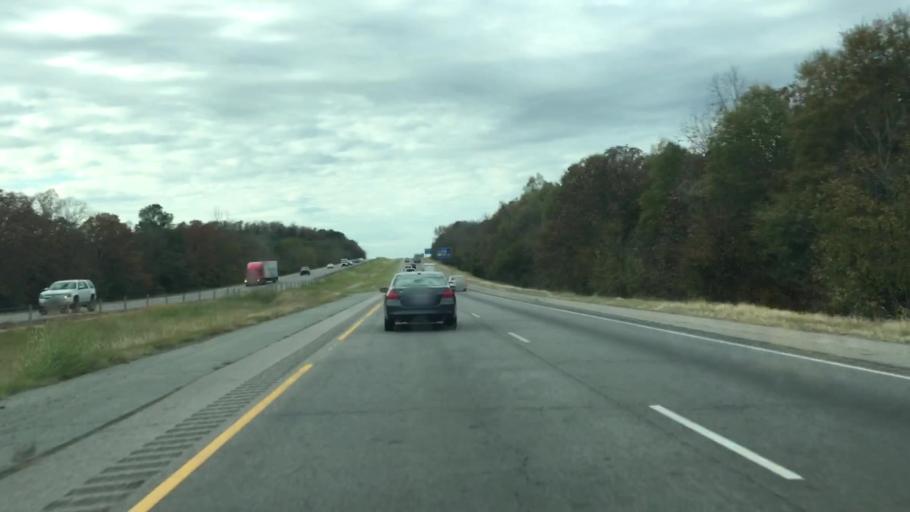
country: US
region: Arkansas
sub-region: Conway County
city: Morrilton
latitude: 35.1676
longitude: -92.6877
